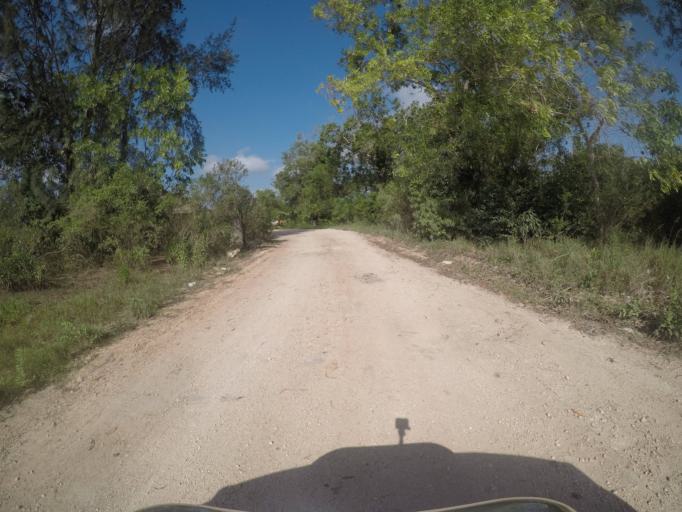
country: TZ
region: Zanzibar Central/South
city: Koani
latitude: -6.2178
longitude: 39.3322
